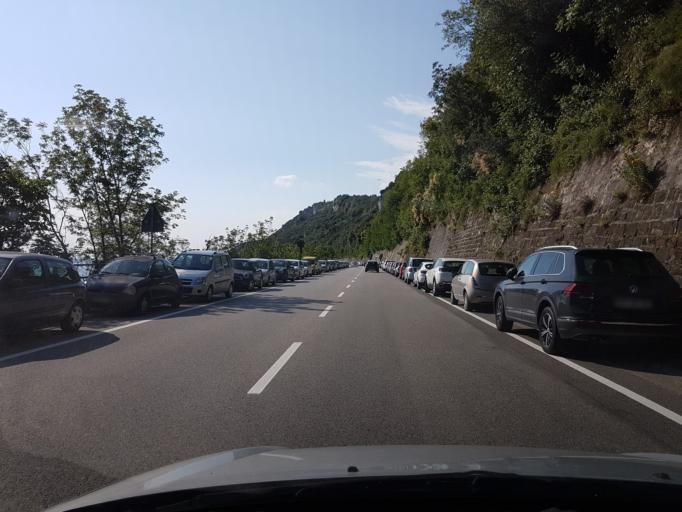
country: IT
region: Friuli Venezia Giulia
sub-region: Provincia di Trieste
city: Aurisina Cave
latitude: 45.7480
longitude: 13.6608
